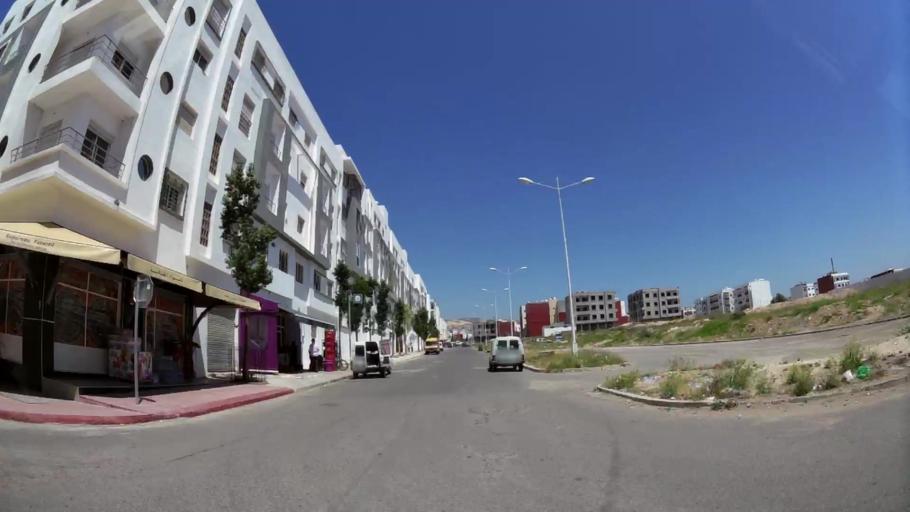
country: MA
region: Oued ed Dahab-Lagouira
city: Dakhla
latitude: 30.4391
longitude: -9.5603
